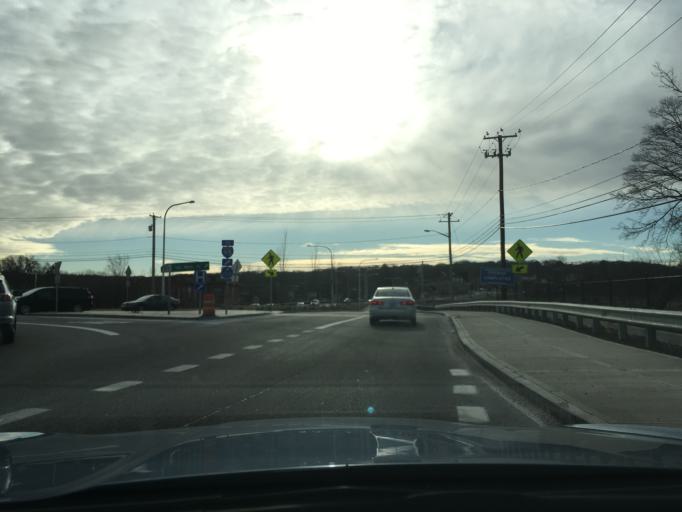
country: US
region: Rhode Island
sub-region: Kent County
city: East Greenwich
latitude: 41.7009
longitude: -71.4600
